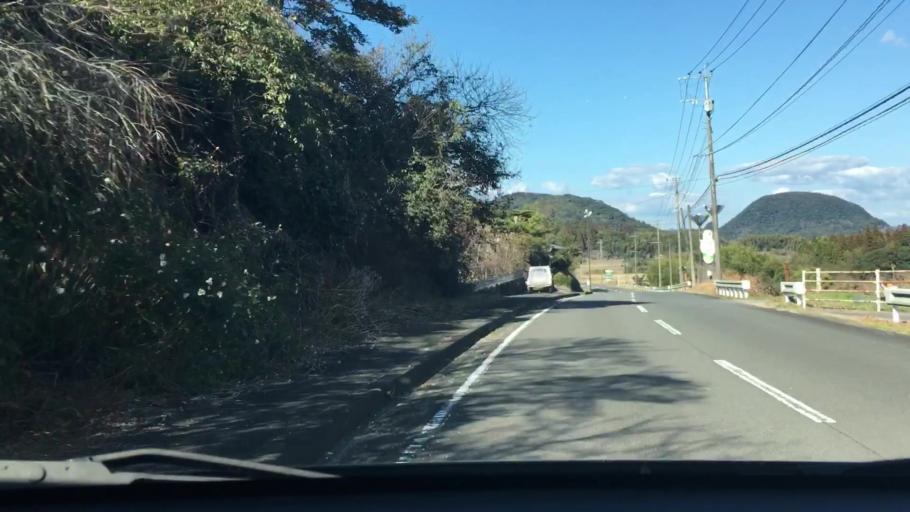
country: JP
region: Kagoshima
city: Satsumasendai
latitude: 31.7726
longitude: 130.4012
